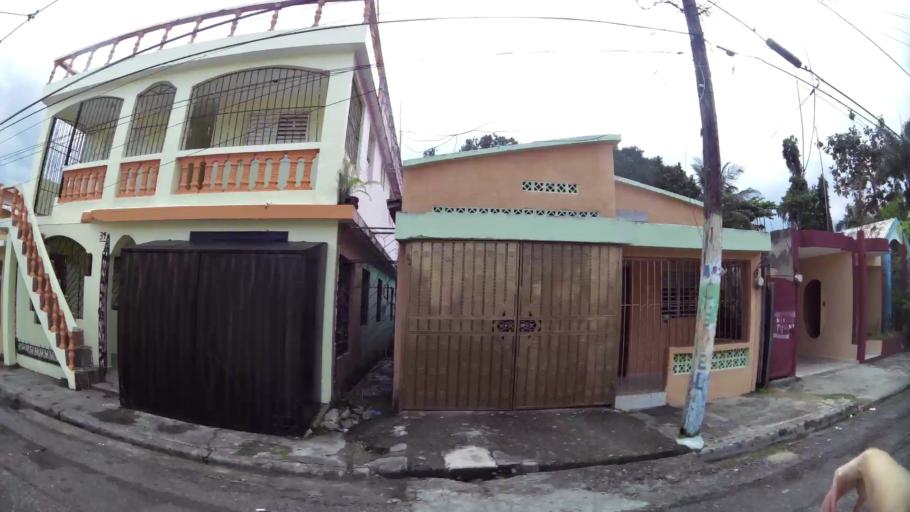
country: DO
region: San Cristobal
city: Villa Altagracia
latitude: 18.6717
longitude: -70.1756
